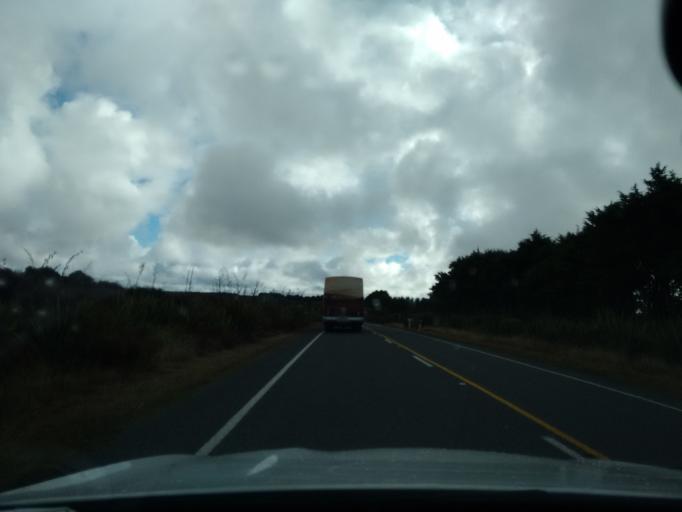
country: NZ
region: Manawatu-Wanganui
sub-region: Ruapehu District
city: Waiouru
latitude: -39.1792
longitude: 175.4581
